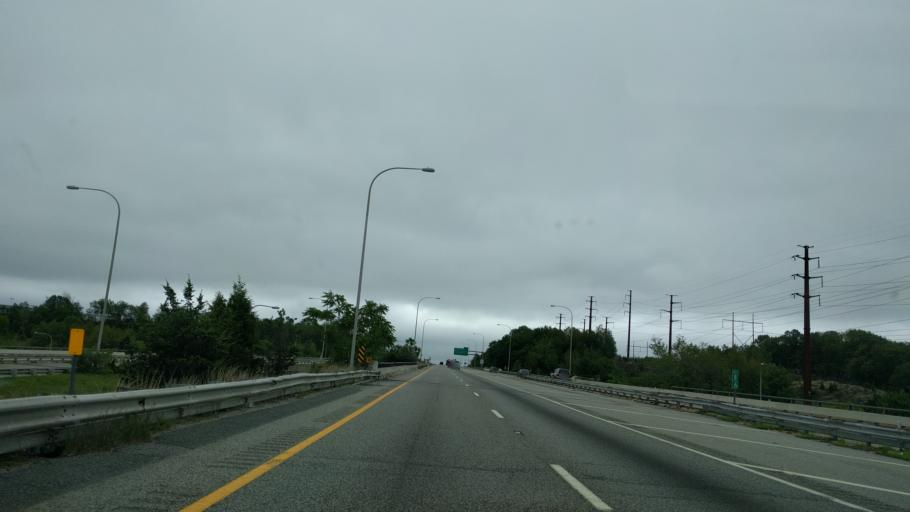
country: US
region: Rhode Island
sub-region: Providence County
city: Johnston
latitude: 41.8213
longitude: -71.5134
